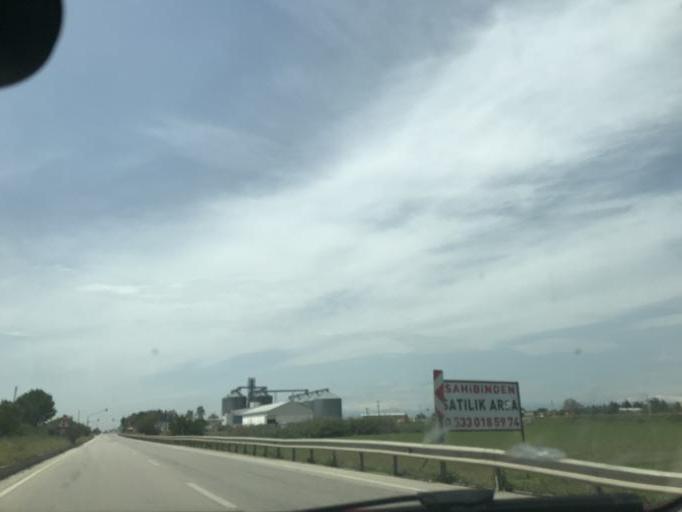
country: TR
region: Adana
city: Yakapinar
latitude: 36.9725
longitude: 35.5126
